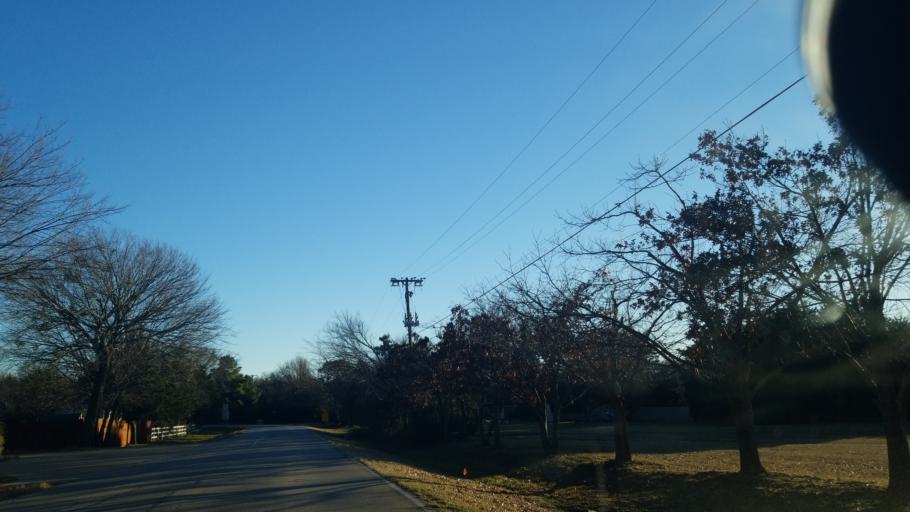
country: US
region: Texas
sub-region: Denton County
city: Shady Shores
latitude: 33.1597
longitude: -97.0403
